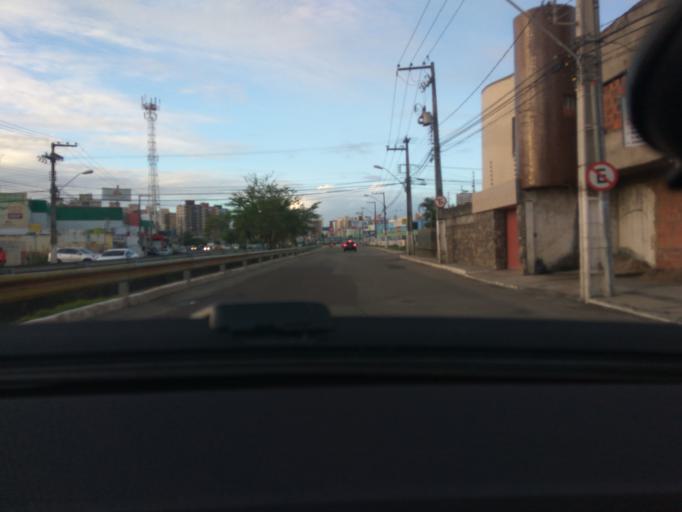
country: BR
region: Sergipe
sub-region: Aracaju
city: Aracaju
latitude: -10.9460
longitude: -37.0627
